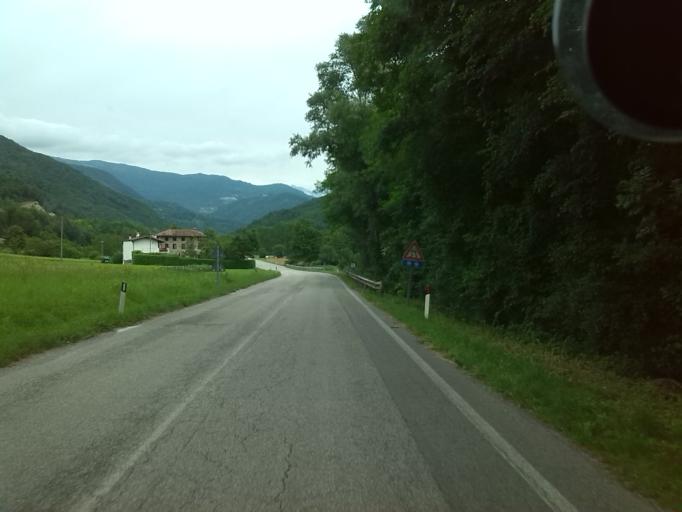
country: IT
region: Friuli Venezia Giulia
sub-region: Provincia di Udine
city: San Pietro al Natisone
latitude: 46.1306
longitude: 13.5000
